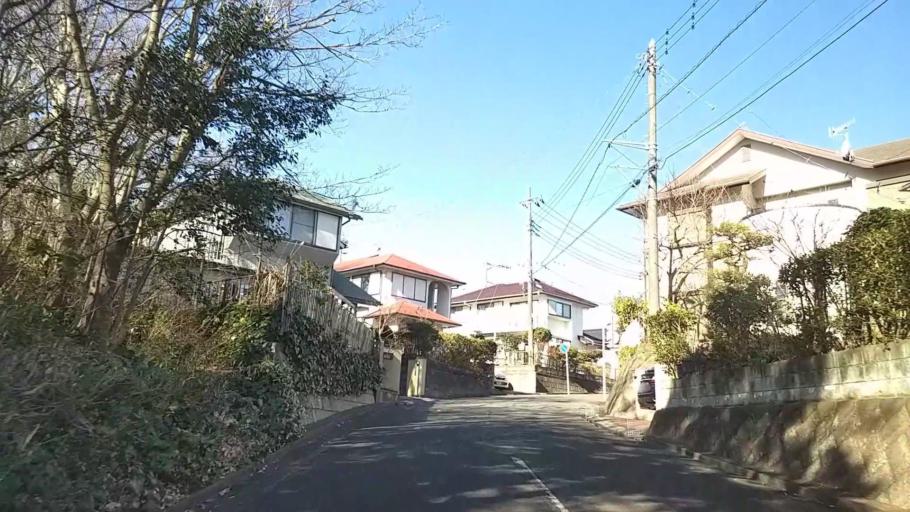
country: JP
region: Kanagawa
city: Hadano
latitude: 35.3833
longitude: 139.2214
